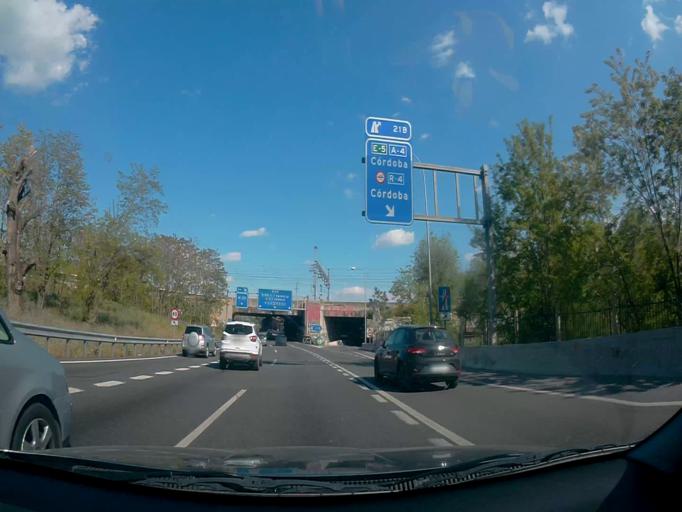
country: ES
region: Madrid
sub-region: Provincia de Madrid
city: Villaverde
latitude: 40.3611
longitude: -3.6813
